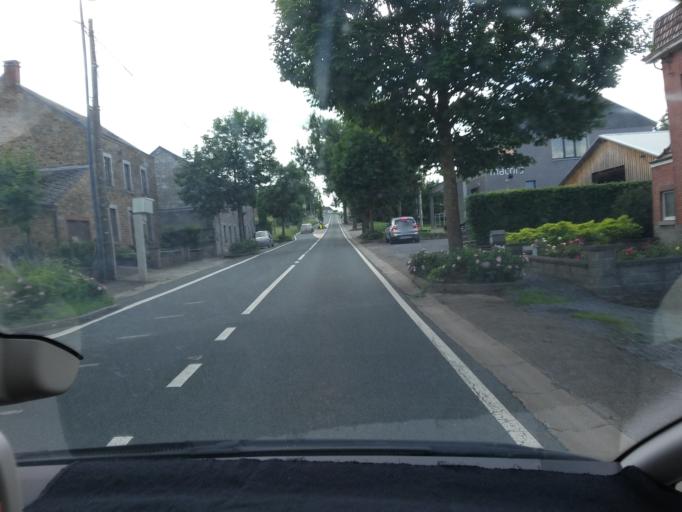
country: BE
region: Wallonia
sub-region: Province de Namur
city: Hamois
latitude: 50.3390
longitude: 5.1543
